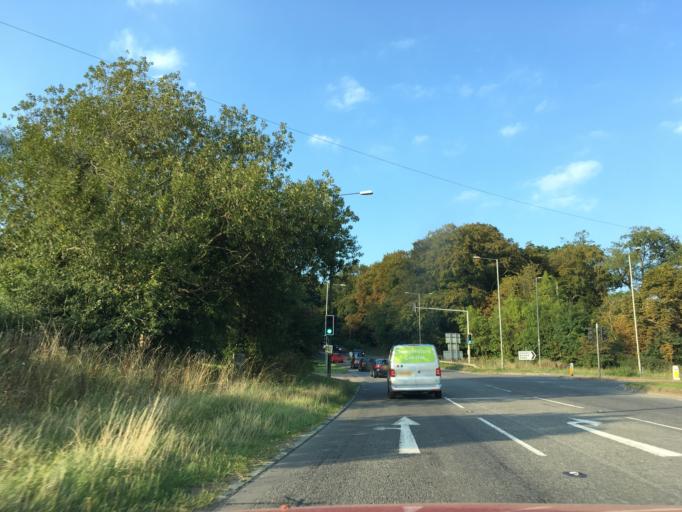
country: GB
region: England
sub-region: Gloucestershire
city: Stow on the Wold
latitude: 51.9173
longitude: -1.7257
